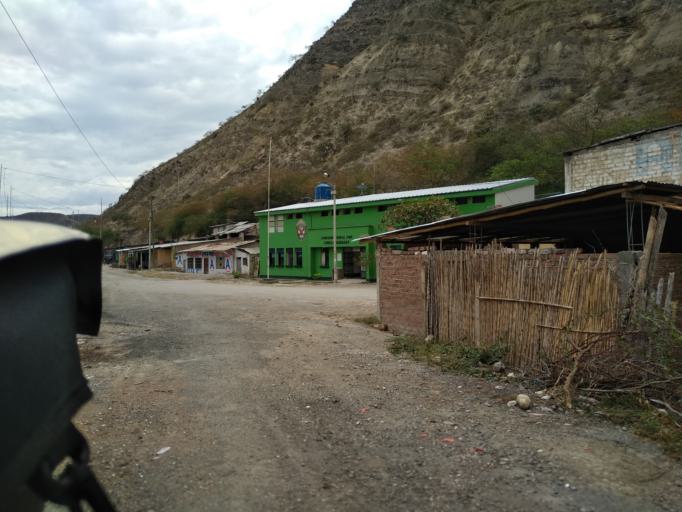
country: PE
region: Cajamarca
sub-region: Provincia de Jaen
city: Bellavista
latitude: -5.7544
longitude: -78.6906
